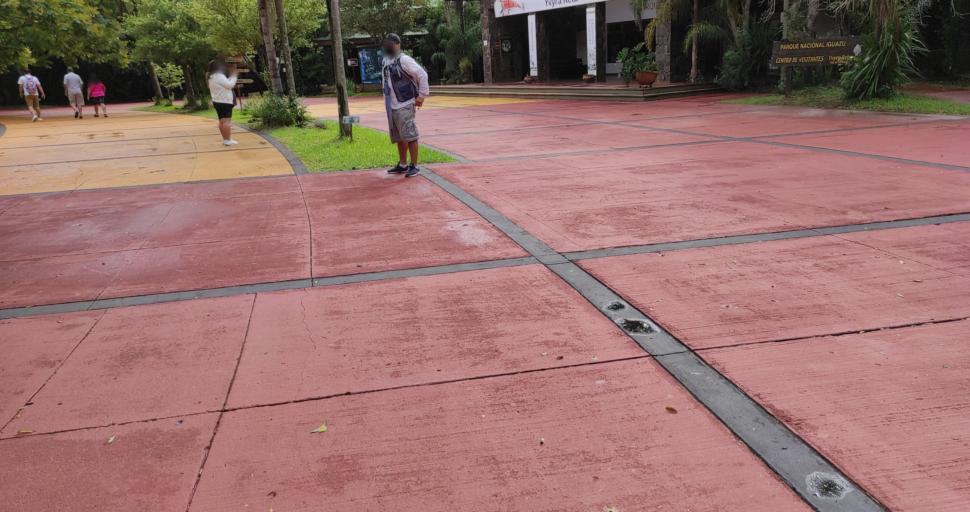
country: AR
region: Misiones
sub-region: Departamento de Iguazu
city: Puerto Iguazu
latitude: -25.6824
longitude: -54.4542
